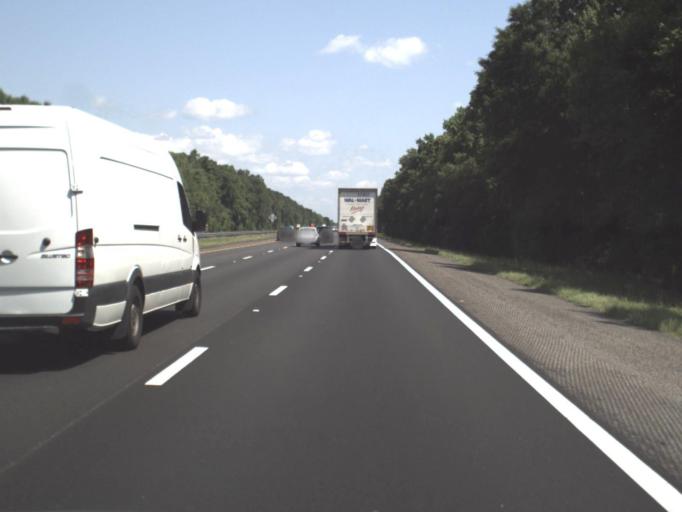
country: US
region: Florida
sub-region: Nassau County
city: Yulee
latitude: 30.5464
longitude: -81.6385
